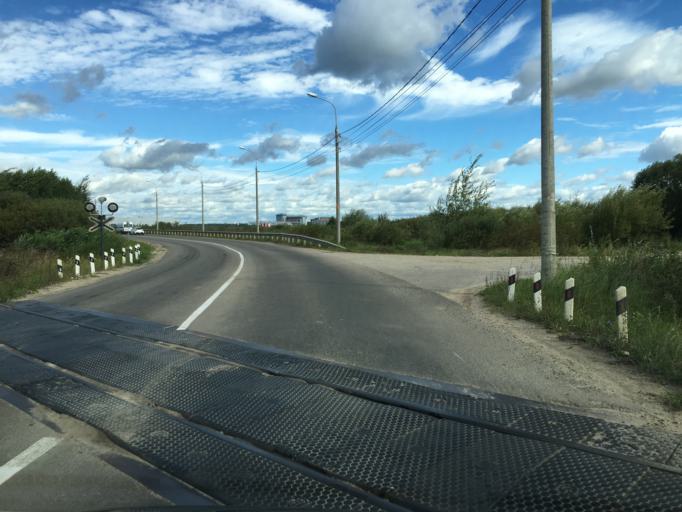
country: RU
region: Kaluga
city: Kaluga
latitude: 54.5560
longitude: 36.3551
